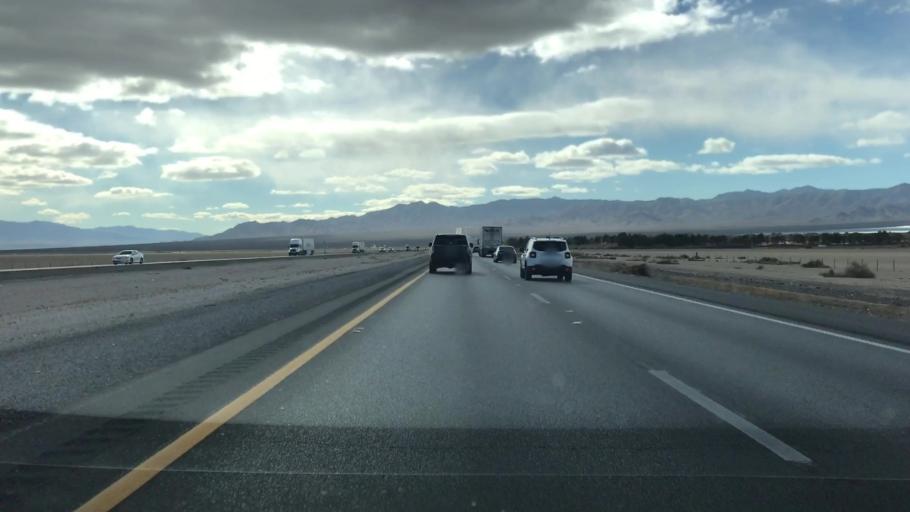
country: US
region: Nevada
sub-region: Clark County
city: Sandy Valley
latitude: 35.5650
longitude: -115.4096
